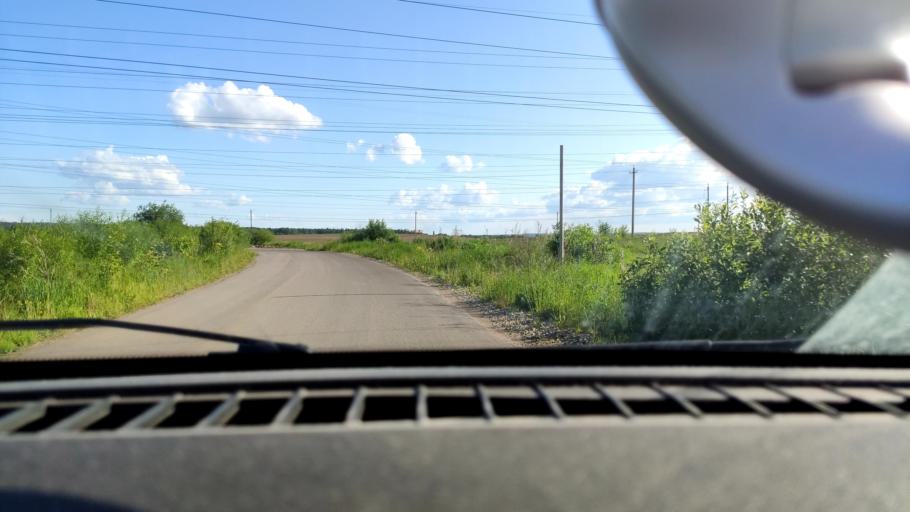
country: RU
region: Perm
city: Ferma
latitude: 57.9164
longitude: 56.3389
